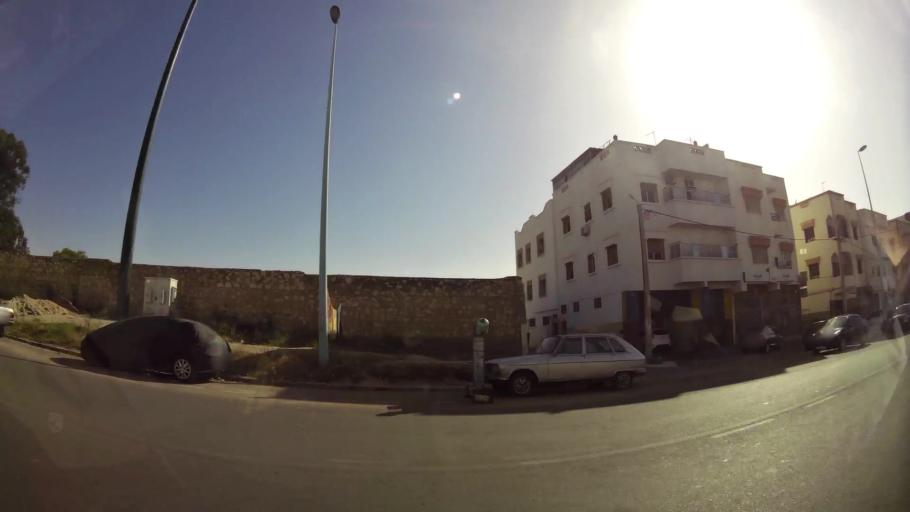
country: MA
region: Oued ed Dahab-Lagouira
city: Dakhla
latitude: 30.4186
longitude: -9.5685
